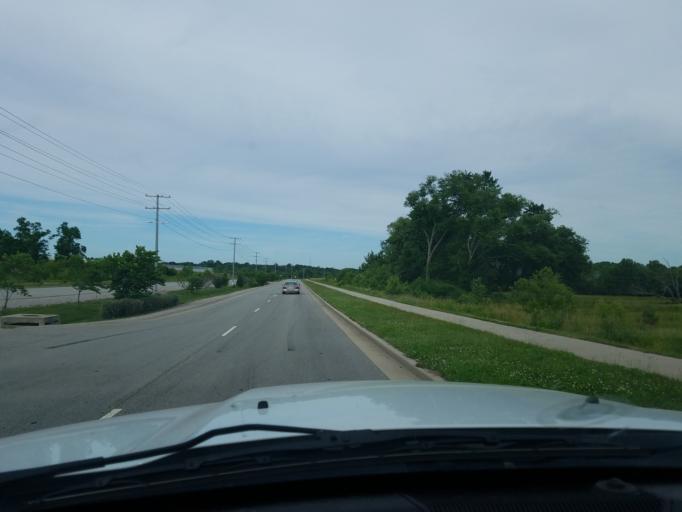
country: US
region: Tennessee
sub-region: Putnam County
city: Baxter
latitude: 36.1346
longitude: -85.5763
